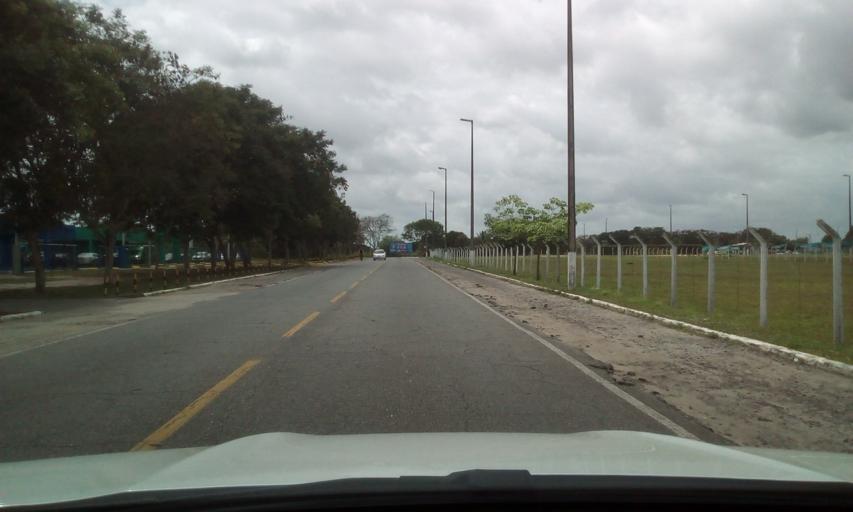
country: BR
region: Paraiba
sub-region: Bayeux
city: Bayeux
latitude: -7.1432
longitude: -34.9485
